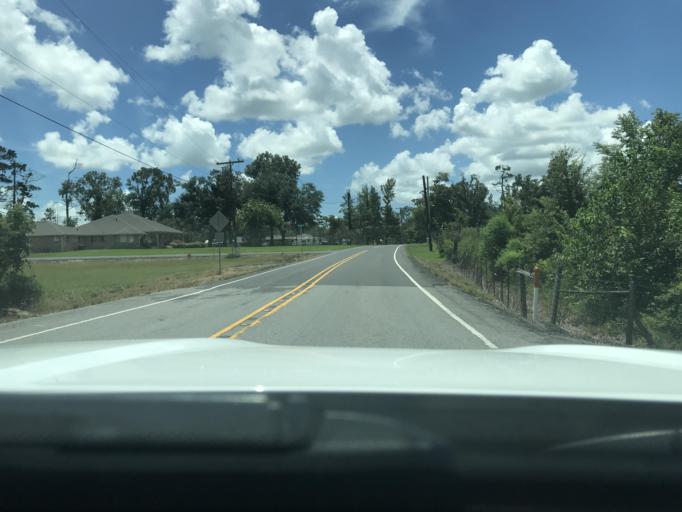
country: US
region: Louisiana
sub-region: Calcasieu Parish
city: Moss Bluff
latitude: 30.3051
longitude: -93.1807
